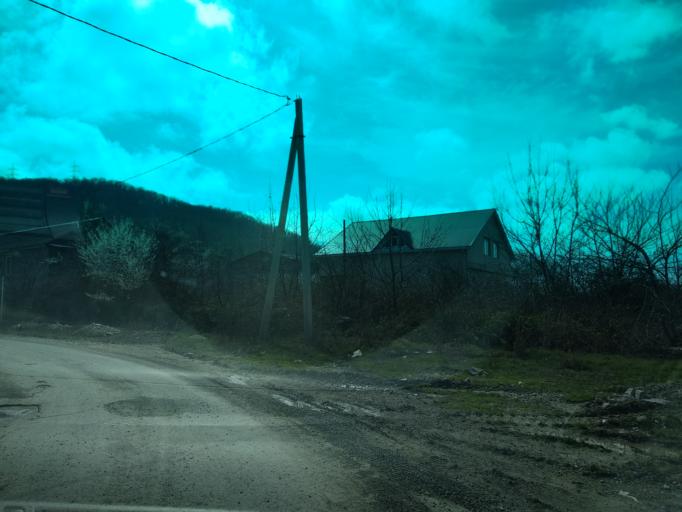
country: RU
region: Krasnodarskiy
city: Shepsi
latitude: 44.0535
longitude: 39.1624
